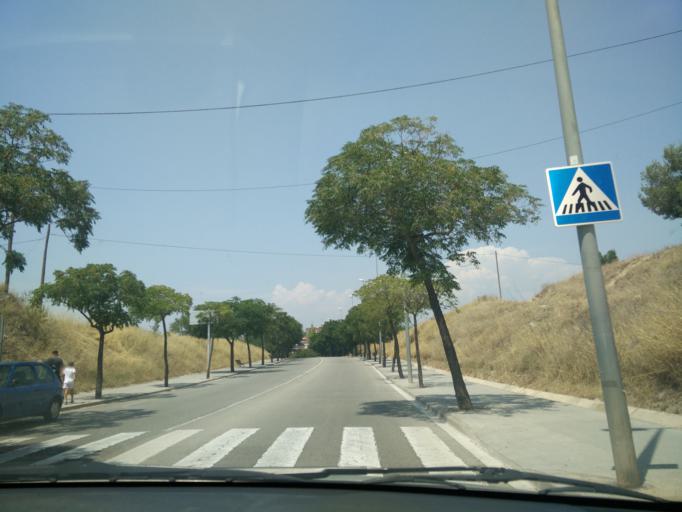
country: ES
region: Catalonia
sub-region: Provincia de Barcelona
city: Manresa
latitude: 41.7239
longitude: 1.8406
